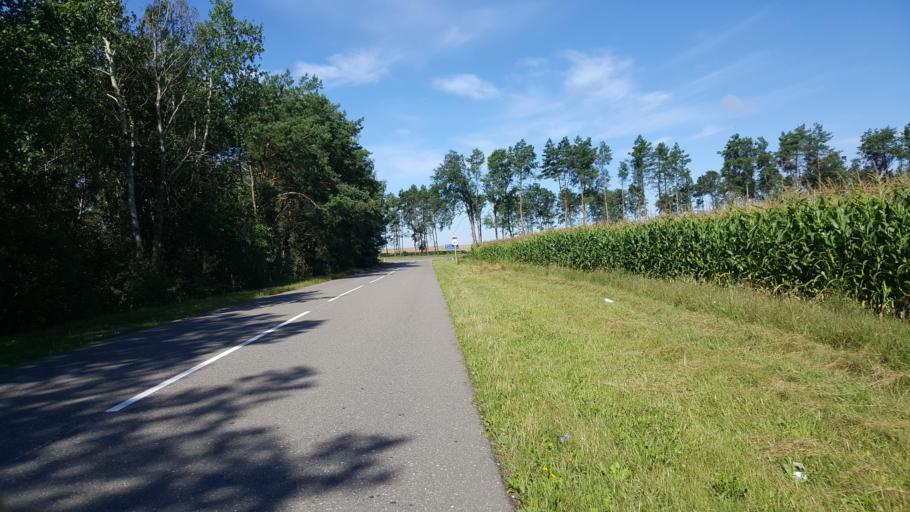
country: BY
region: Brest
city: Charnawchytsy
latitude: 52.2894
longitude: 23.7772
